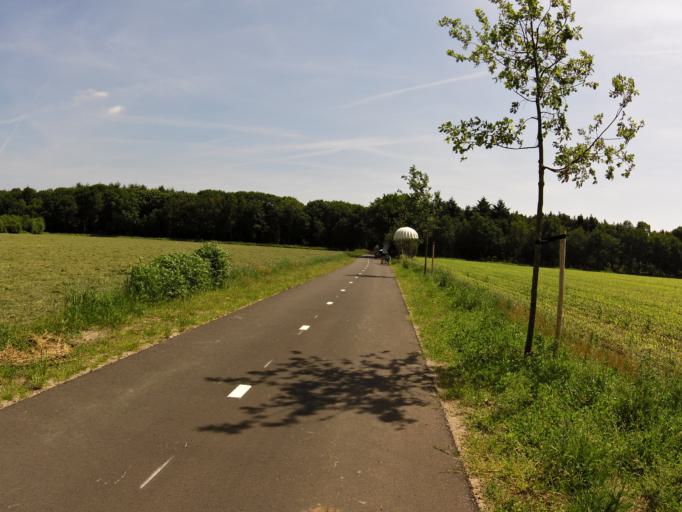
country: NL
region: North Brabant
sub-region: Gemeente Son en Breugel
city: Son
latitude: 51.5247
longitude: 5.4637
